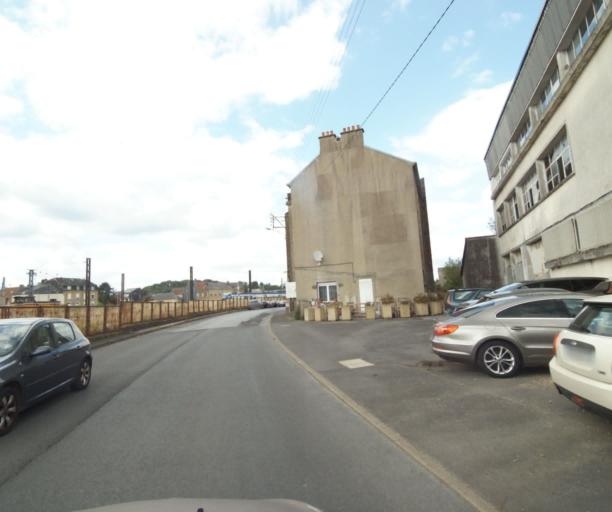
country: FR
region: Champagne-Ardenne
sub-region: Departement des Ardennes
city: Charleville-Mezieres
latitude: 49.7693
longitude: 4.7281
